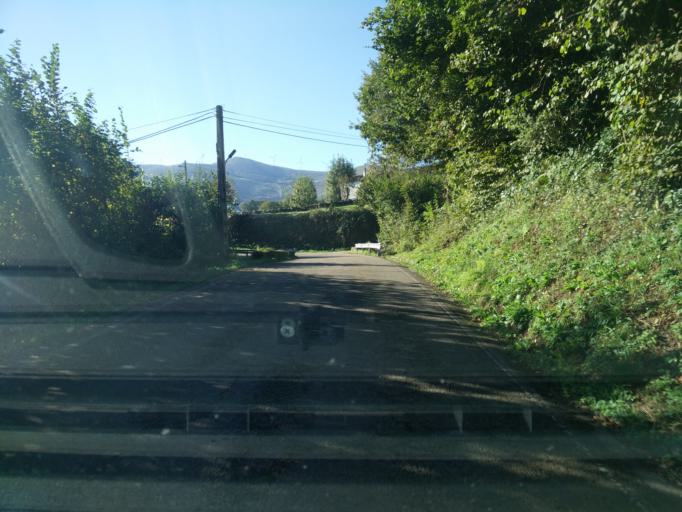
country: ES
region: Cantabria
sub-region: Provincia de Cantabria
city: San Pedro del Romeral
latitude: 43.1157
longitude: -3.8078
